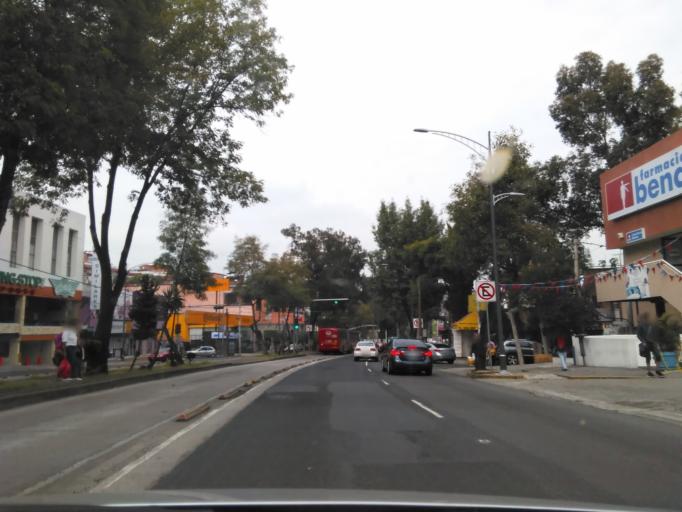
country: MX
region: Mexico City
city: Tlalpan
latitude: 19.2844
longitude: -99.1757
